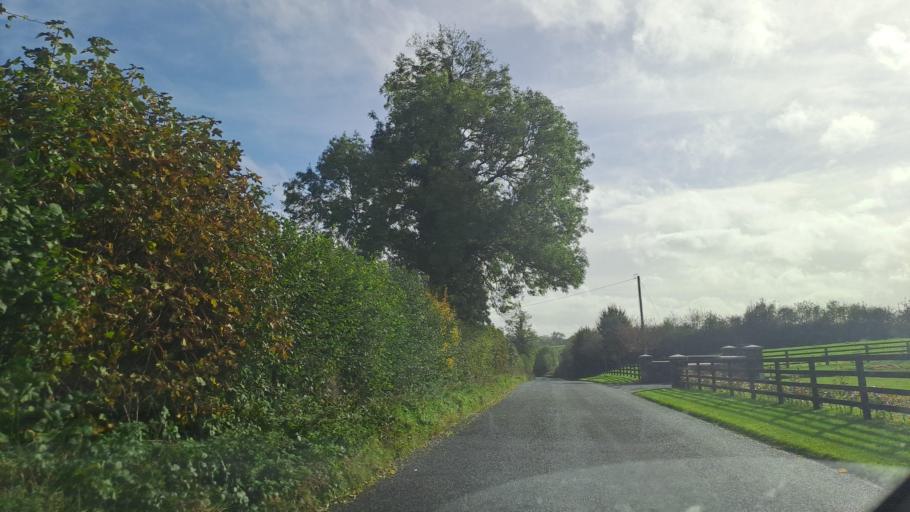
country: IE
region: Ulster
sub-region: County Monaghan
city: Carrickmacross
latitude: 53.8881
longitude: -6.6934
